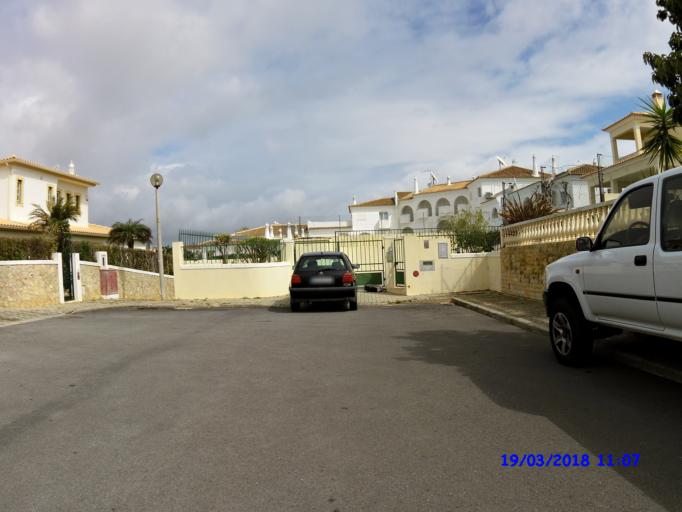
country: PT
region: Faro
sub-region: Albufeira
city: Guia
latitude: 37.0786
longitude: -8.3005
